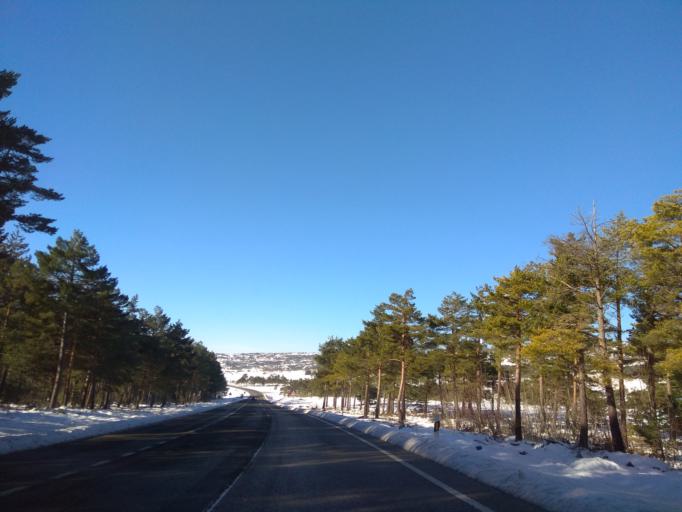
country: ES
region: Castille and Leon
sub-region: Provincia de Burgos
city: Espinosa de los Monteros
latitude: 42.9419
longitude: -3.6742
